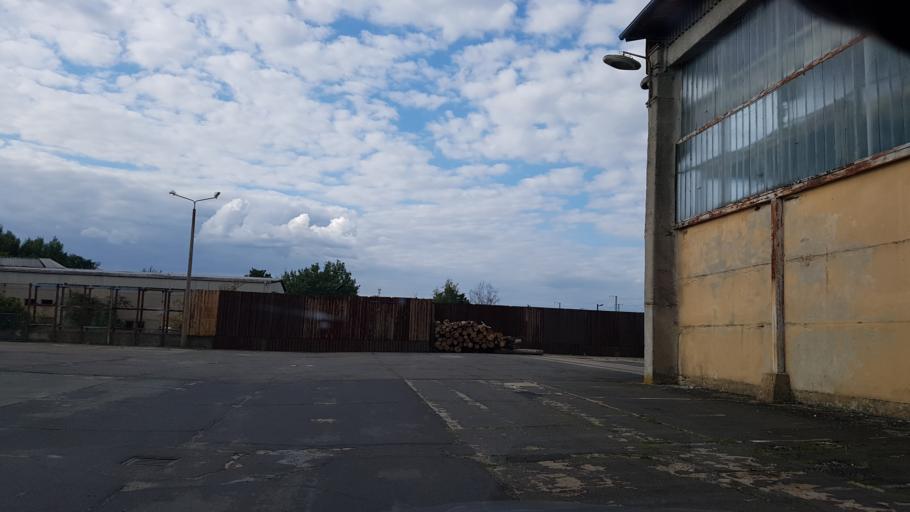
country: DE
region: Brandenburg
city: Falkenberg
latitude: 51.5930
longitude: 13.2415
